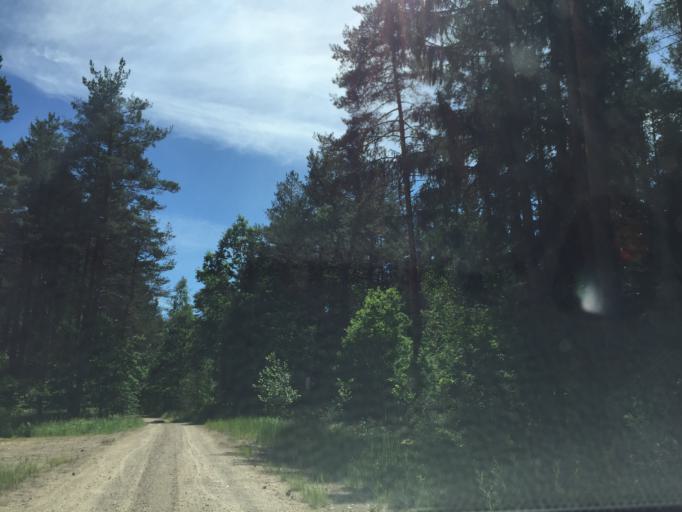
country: LV
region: Kuldigas Rajons
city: Kuldiga
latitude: 57.1009
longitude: 21.8926
